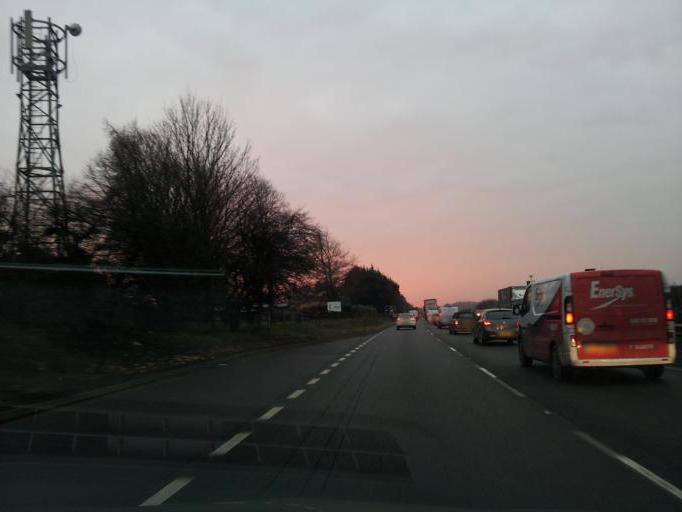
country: GB
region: England
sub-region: Peterborough
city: Thornhaugh
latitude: 52.5978
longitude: -0.4207
